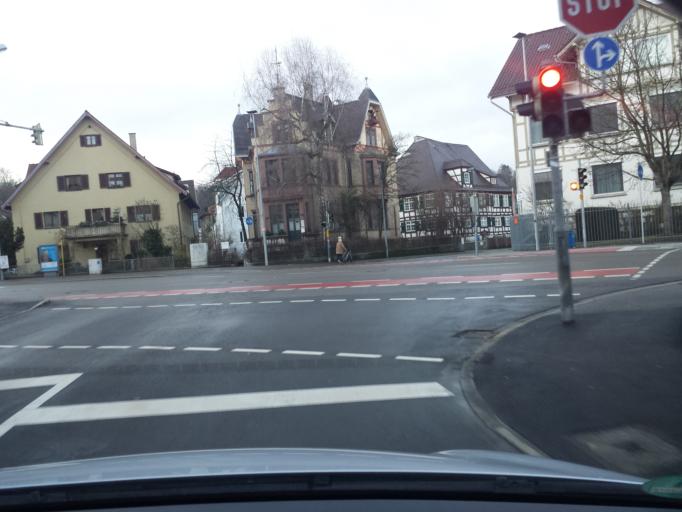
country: DE
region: Baden-Wuerttemberg
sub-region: Tuebingen Region
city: Biberach an der Riss
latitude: 48.1009
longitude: 9.7890
